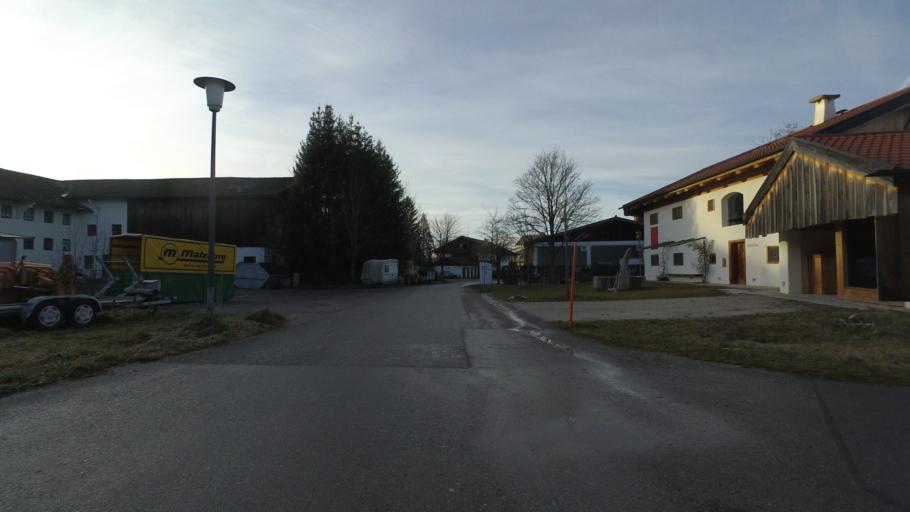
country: DE
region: Bavaria
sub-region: Upper Bavaria
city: Chieming
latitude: 47.8894
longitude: 12.5427
